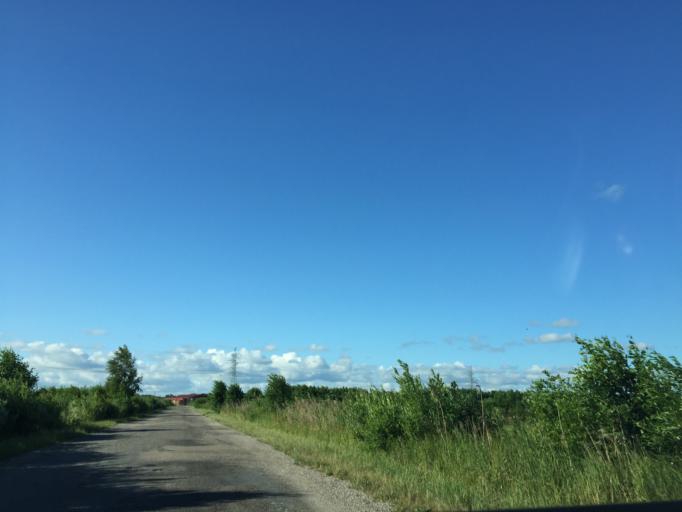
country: LV
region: Ventspils
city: Ventspils
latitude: 57.4020
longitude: 21.6486
